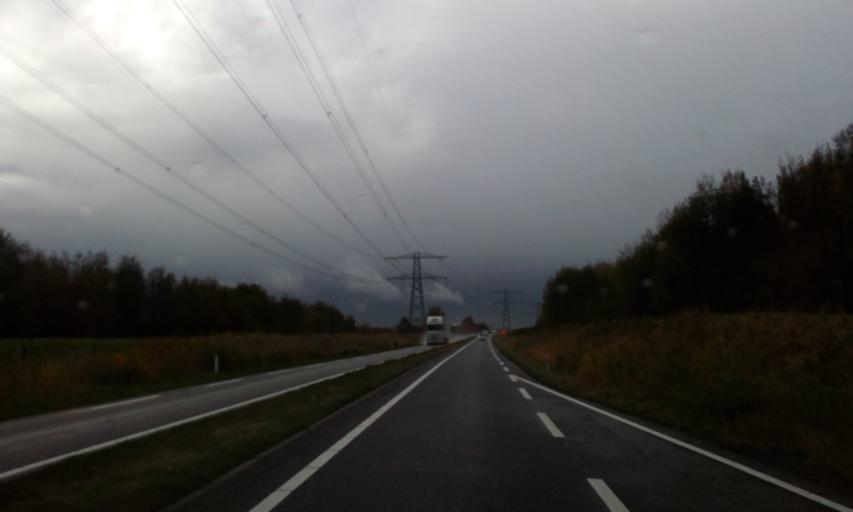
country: NL
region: South Holland
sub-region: Gemeente Westland
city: De Lier
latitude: 51.9922
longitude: 4.2519
